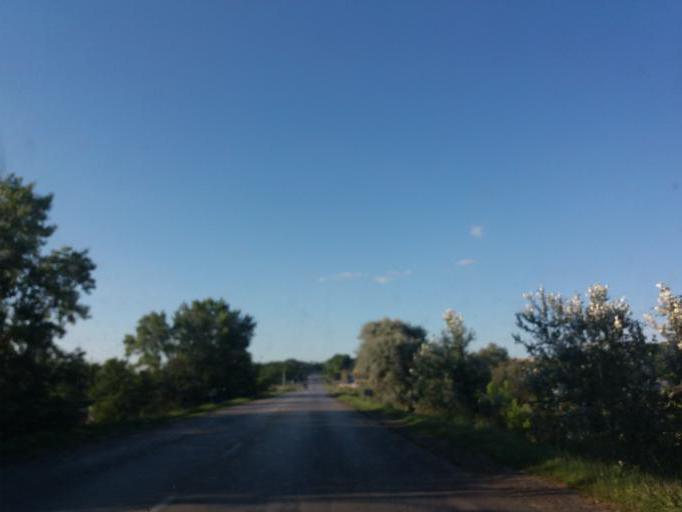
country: HU
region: Fejer
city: Baracska
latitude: 47.2897
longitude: 18.7584
